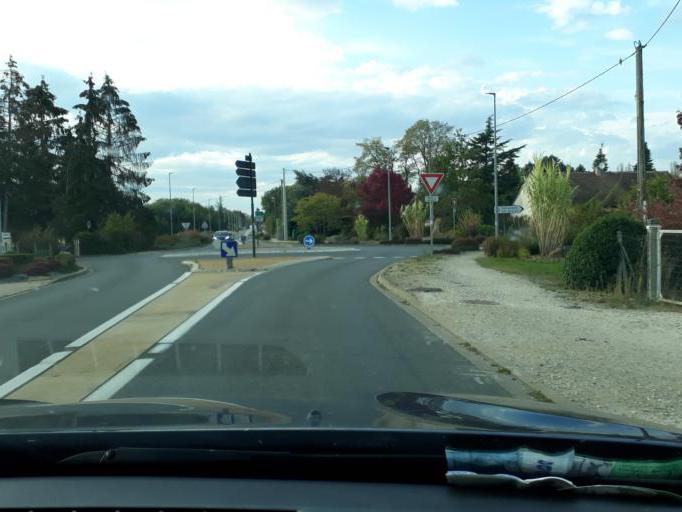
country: FR
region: Centre
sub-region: Departement du Loiret
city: Chateauneuf-sur-Loire
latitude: 47.8583
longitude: 2.2637
